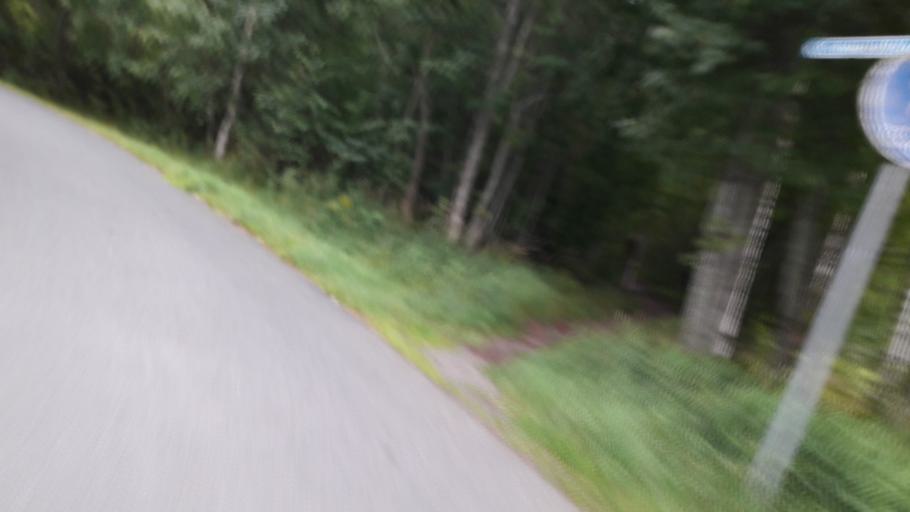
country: FI
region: North Karelia
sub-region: Joensuu
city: Joensuu
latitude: 62.6173
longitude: 29.6944
